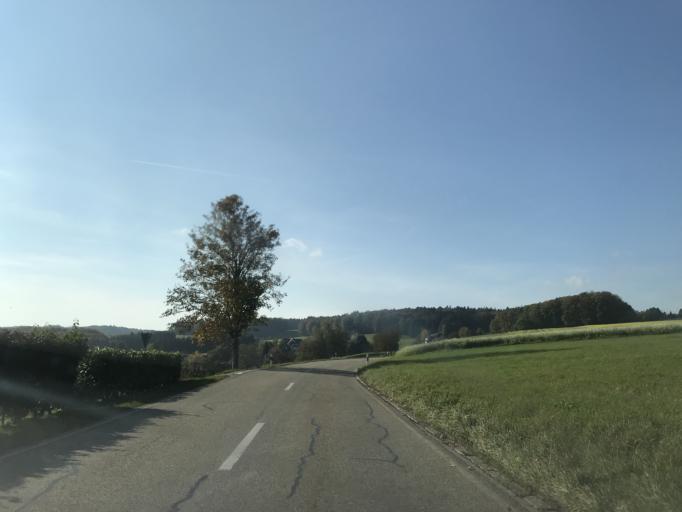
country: DE
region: Baden-Wuerttemberg
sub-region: Freiburg Region
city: Gorwihl
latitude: 47.6334
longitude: 8.0694
